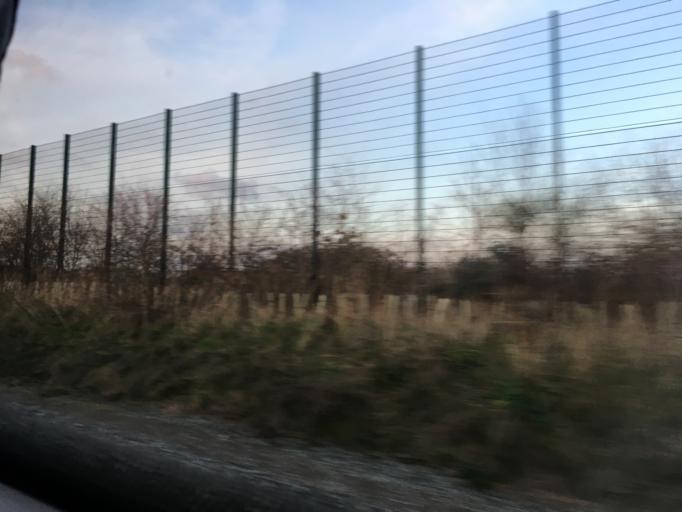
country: GB
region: England
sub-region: Manchester
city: Chorlton cum Hardy
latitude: 53.4340
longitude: -2.2527
